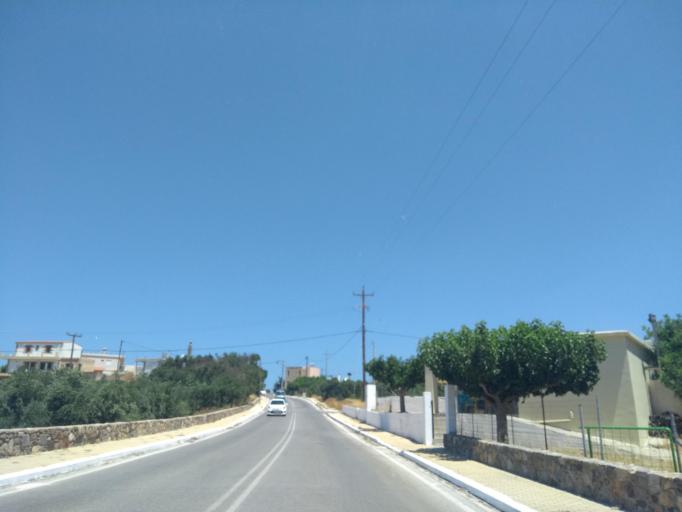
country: GR
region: Crete
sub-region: Nomos Chanias
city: Vryses
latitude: 35.3073
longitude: 23.5375
